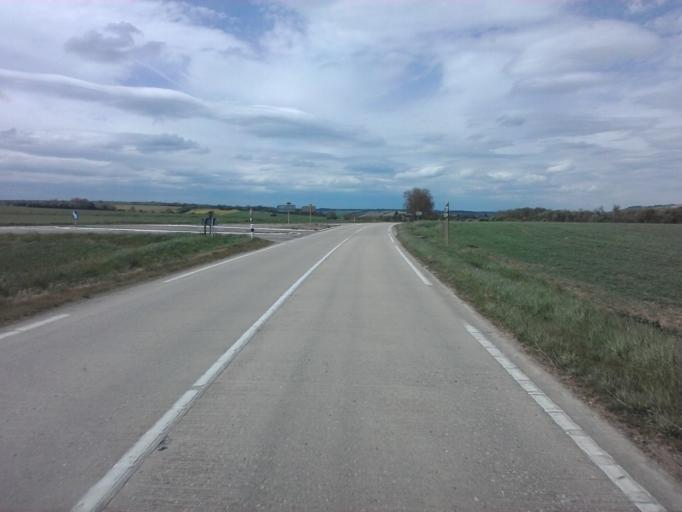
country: FR
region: Bourgogne
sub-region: Departement de l'Yonne
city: Saint-Bris-le-Vineux
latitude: 47.6903
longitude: 3.6498
